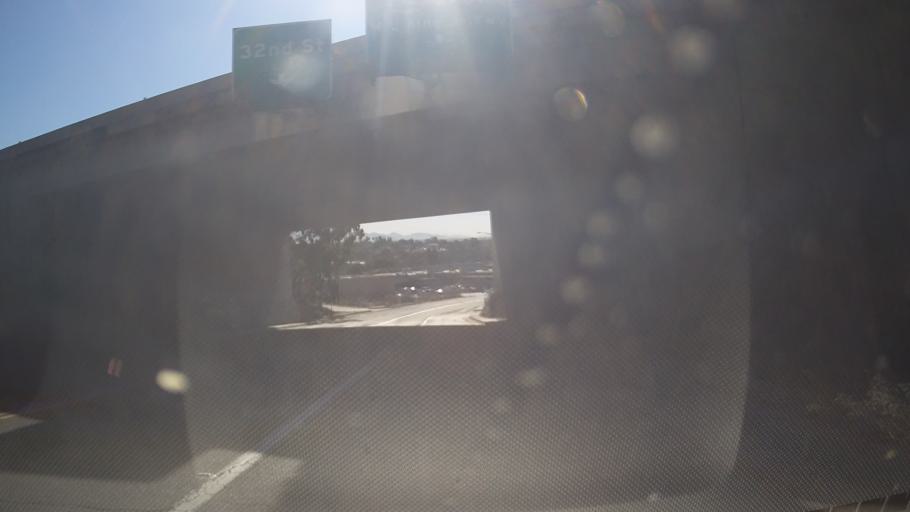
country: US
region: California
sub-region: San Diego County
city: San Diego
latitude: 32.7161
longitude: -117.1246
